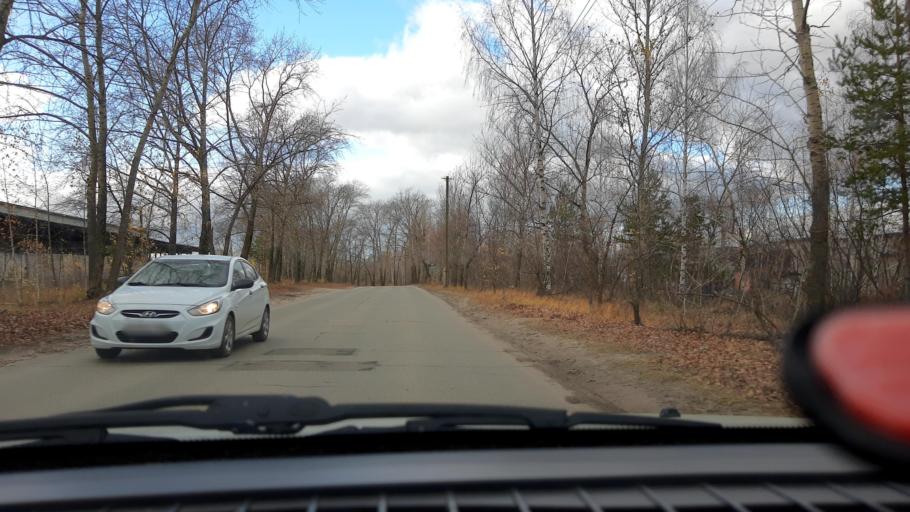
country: RU
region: Nizjnij Novgorod
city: Gorbatovka
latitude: 56.3571
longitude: 43.8032
